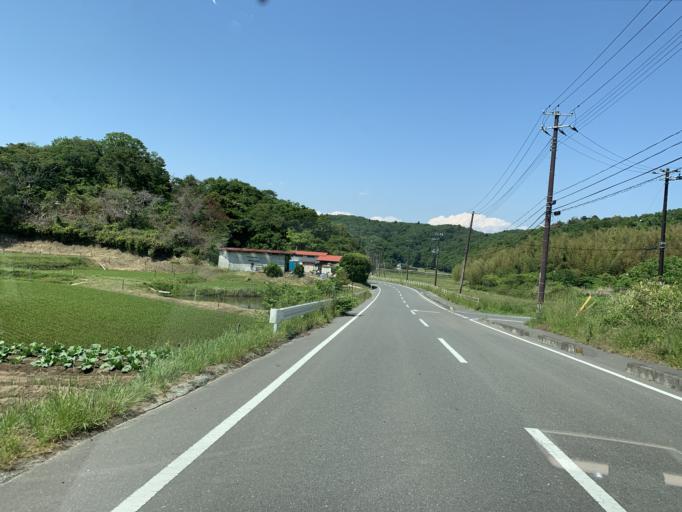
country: JP
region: Miyagi
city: Matsushima
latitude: 38.3277
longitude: 141.1553
